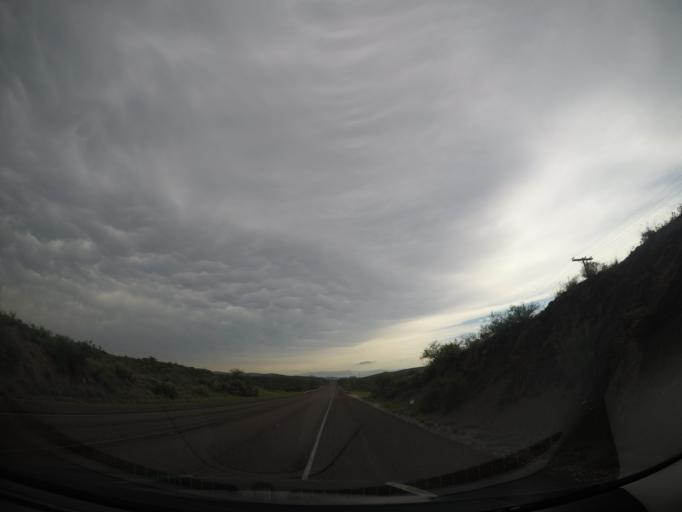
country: US
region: Texas
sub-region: Terrell County
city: Sanderson
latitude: 30.2048
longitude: -102.9728
